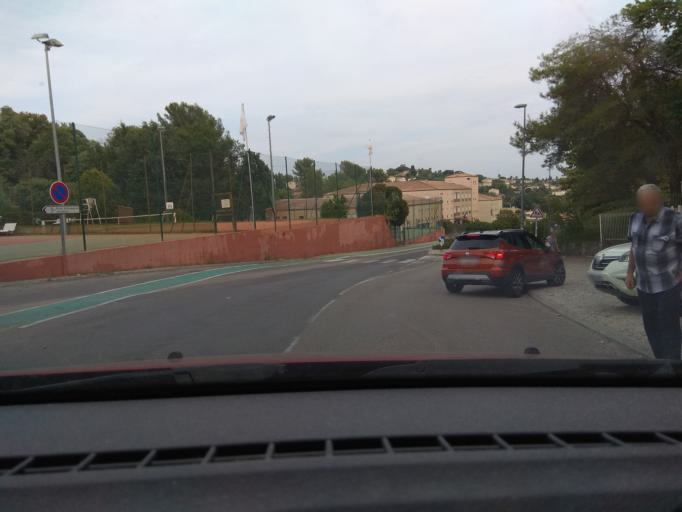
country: FR
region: Provence-Alpes-Cote d'Azur
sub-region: Departement des Alpes-Maritimes
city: La Colle-sur-Loup
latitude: 43.6850
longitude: 7.1012
